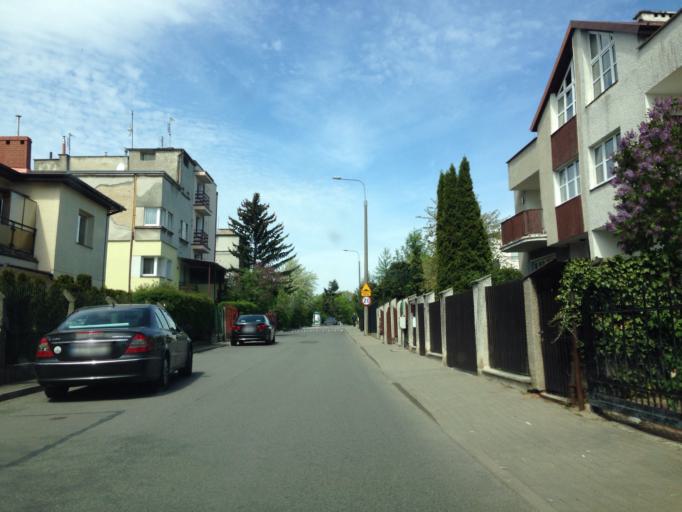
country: PL
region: Pomeranian Voivodeship
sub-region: Gdynia
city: Gdynia
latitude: 54.5134
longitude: 18.5459
